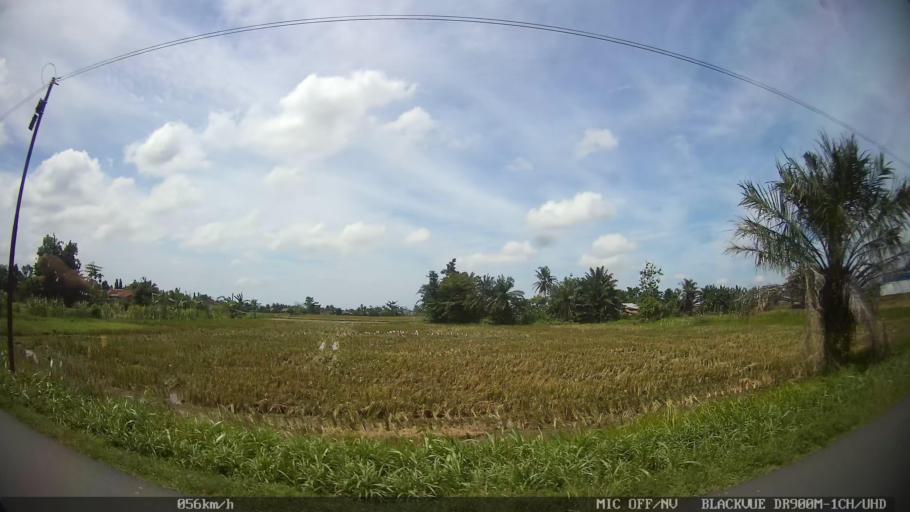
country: ID
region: North Sumatra
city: Percut
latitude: 3.5892
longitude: 98.8734
